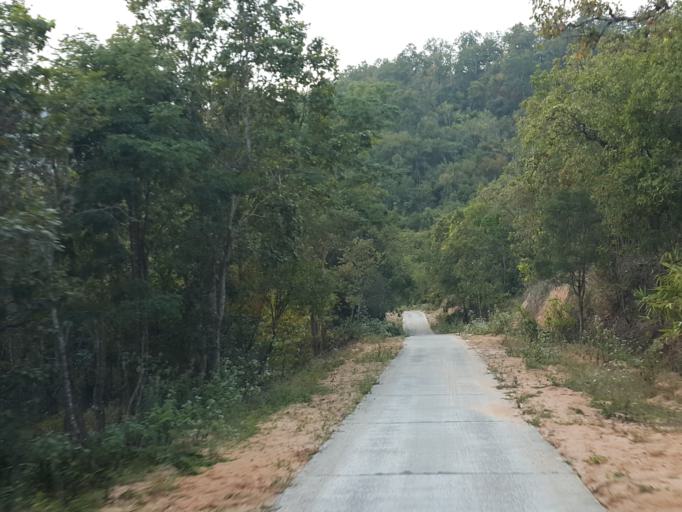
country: TH
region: Chiang Mai
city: Om Koi
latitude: 17.7991
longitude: 98.3128
